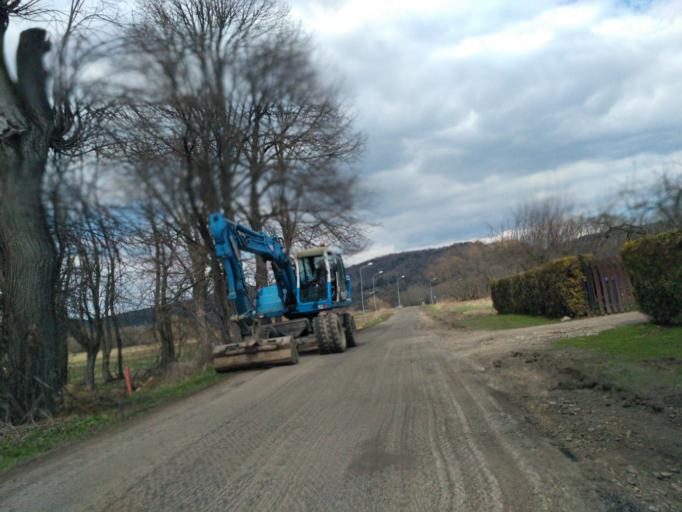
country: PL
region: Subcarpathian Voivodeship
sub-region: Powiat sanocki
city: Tyrawa Woloska
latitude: 49.6484
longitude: 22.2984
